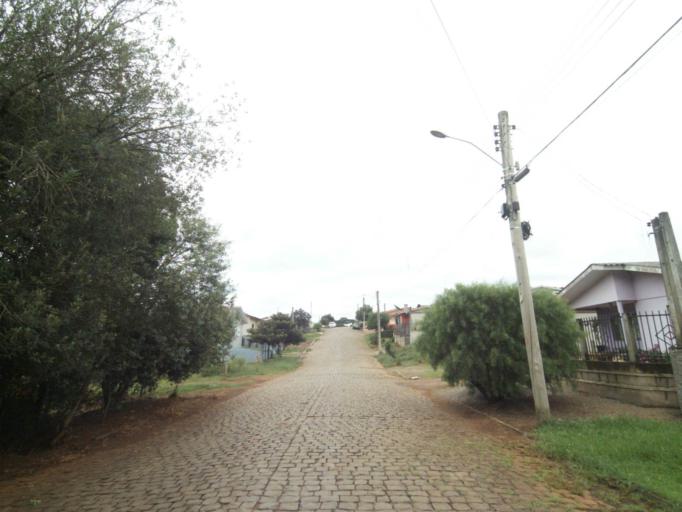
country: BR
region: Rio Grande do Sul
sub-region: Lagoa Vermelha
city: Lagoa Vermelha
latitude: -28.2169
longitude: -51.5301
